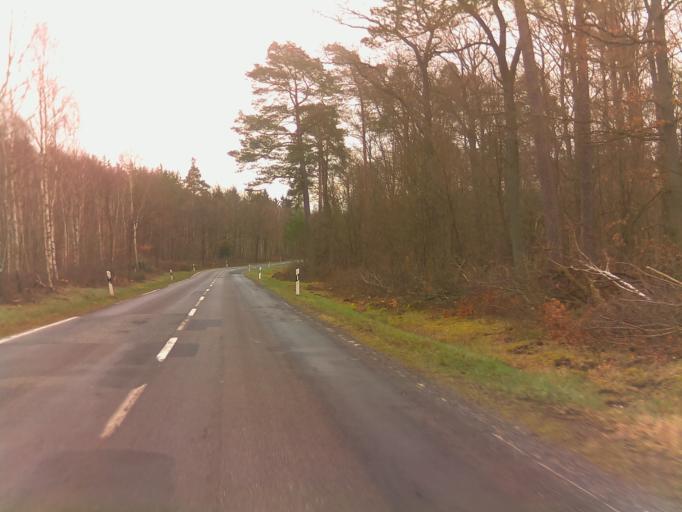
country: DE
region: Rheinland-Pfalz
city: Ippenschied
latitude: 49.8702
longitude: 7.6043
